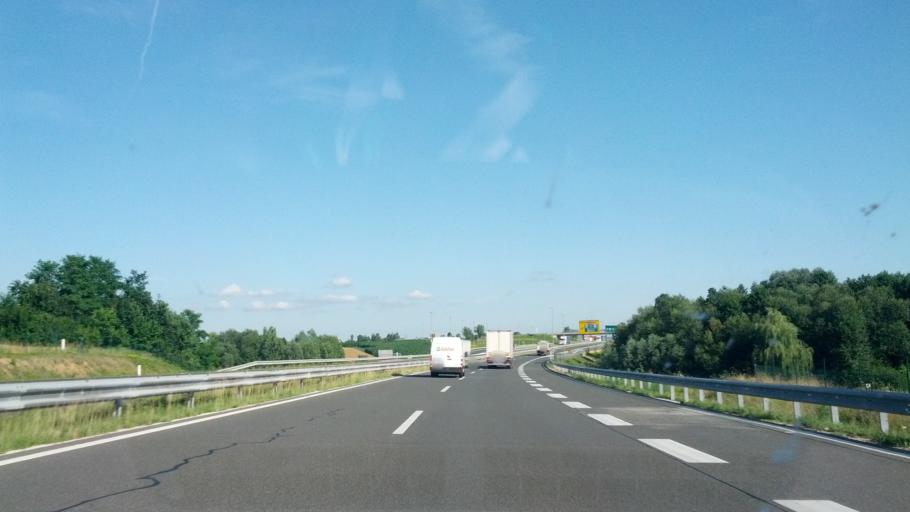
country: HR
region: Zagrebacka
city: Bregana
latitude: 45.8612
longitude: 15.6808
